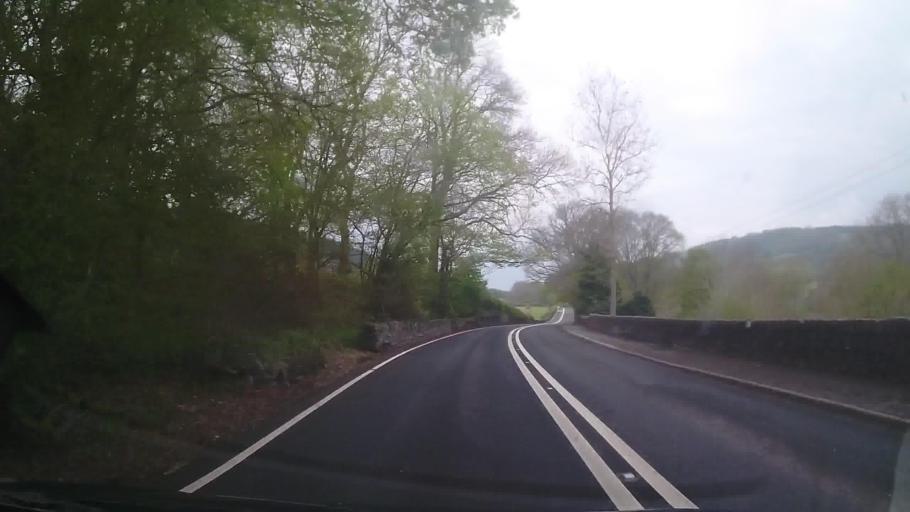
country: GB
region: Wales
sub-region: Denbighshire
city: Corwen
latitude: 52.9770
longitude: -3.3314
